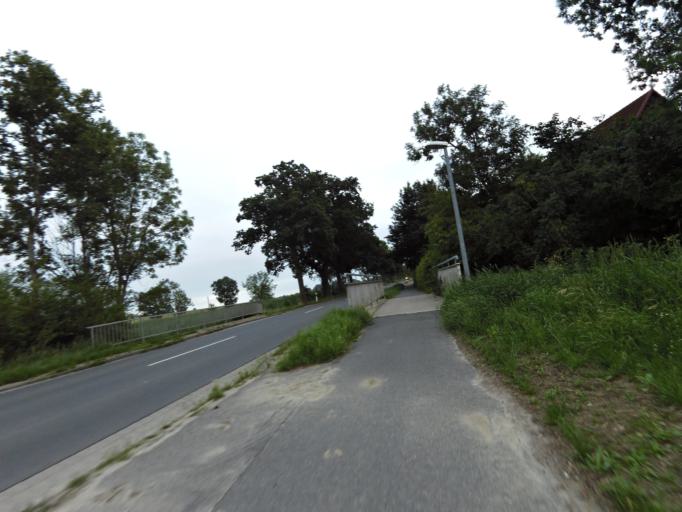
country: DE
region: Lower Saxony
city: Padingbuttel
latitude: 53.7150
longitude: 8.5492
